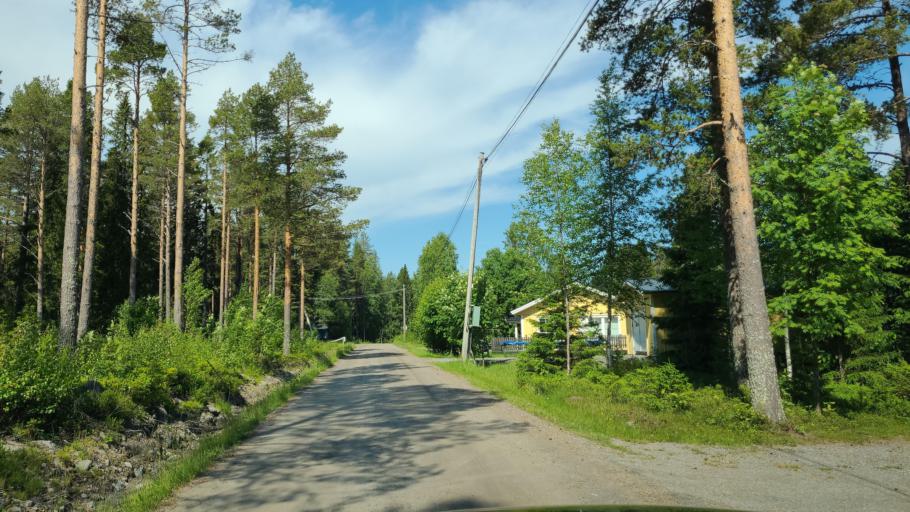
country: SE
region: Vaesterbotten
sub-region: Robertsfors Kommun
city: Robertsfors
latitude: 64.1436
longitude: 20.9622
